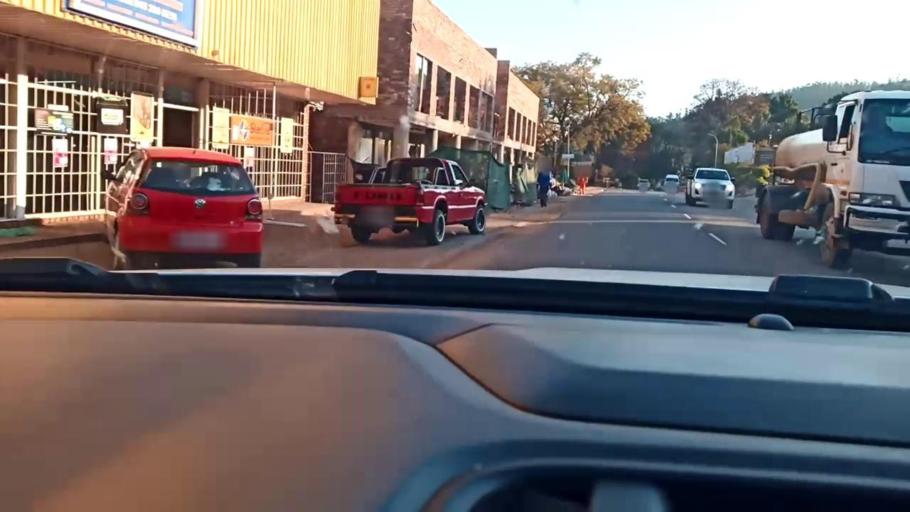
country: ZA
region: Limpopo
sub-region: Mopani District Municipality
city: Duiwelskloof
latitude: -23.6976
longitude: 30.1386
